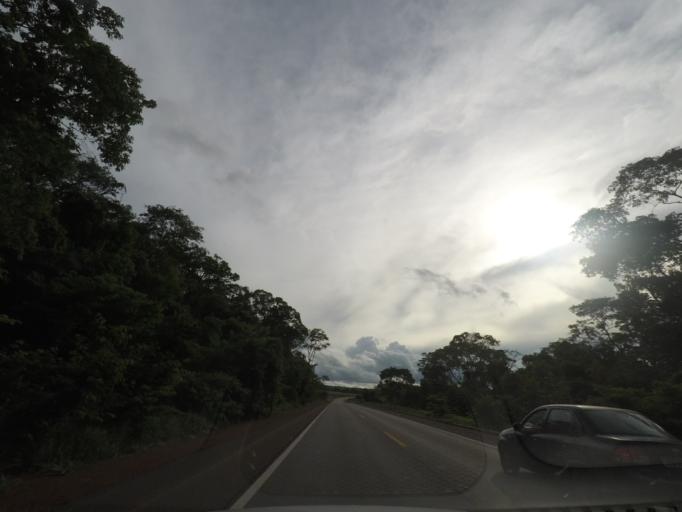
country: BR
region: Goias
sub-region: Pirenopolis
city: Pirenopolis
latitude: -15.6664
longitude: -48.6897
